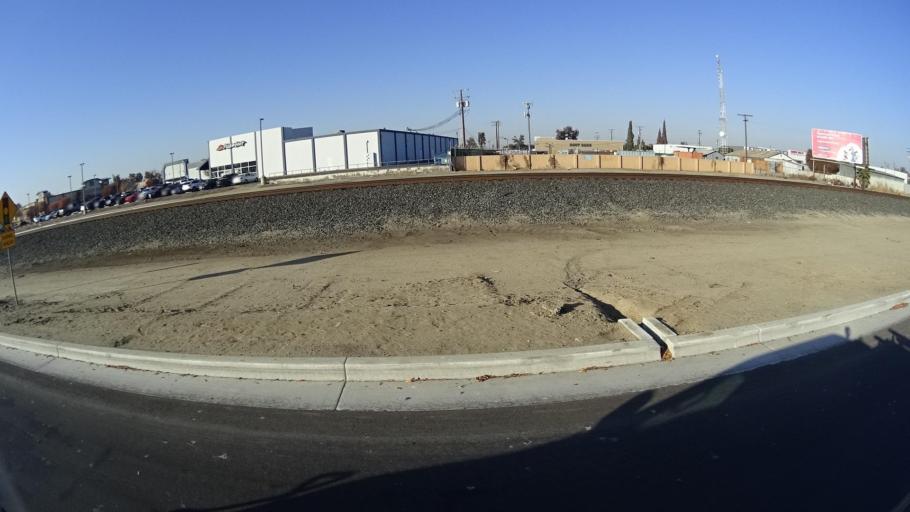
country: US
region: California
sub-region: Kern County
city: Delano
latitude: 35.7775
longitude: -119.2497
